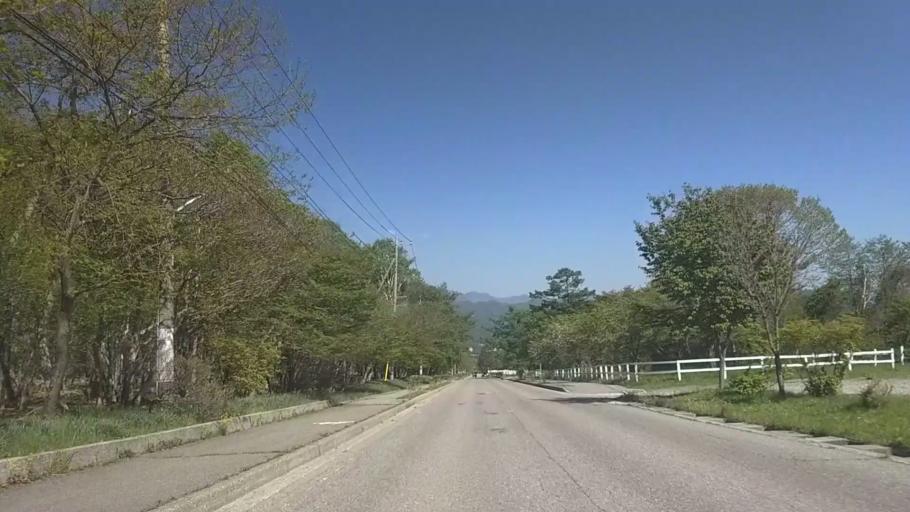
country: JP
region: Yamanashi
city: Nirasaki
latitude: 35.9242
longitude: 138.4229
